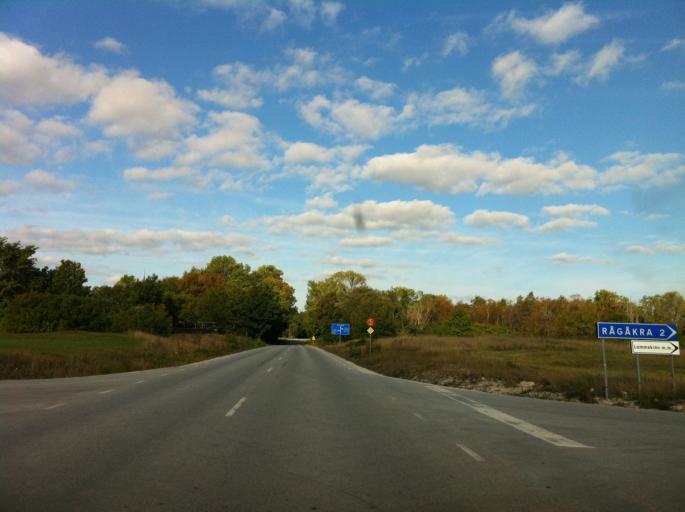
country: SE
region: Gotland
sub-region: Gotland
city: Slite
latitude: 57.4443
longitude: 18.7191
